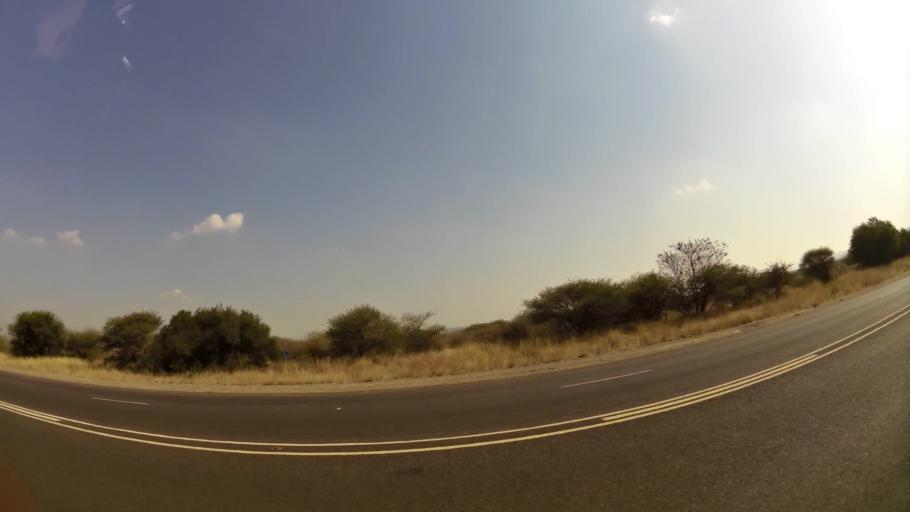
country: ZA
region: North-West
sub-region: Bojanala Platinum District Municipality
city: Mogwase
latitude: -25.3970
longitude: 27.0721
